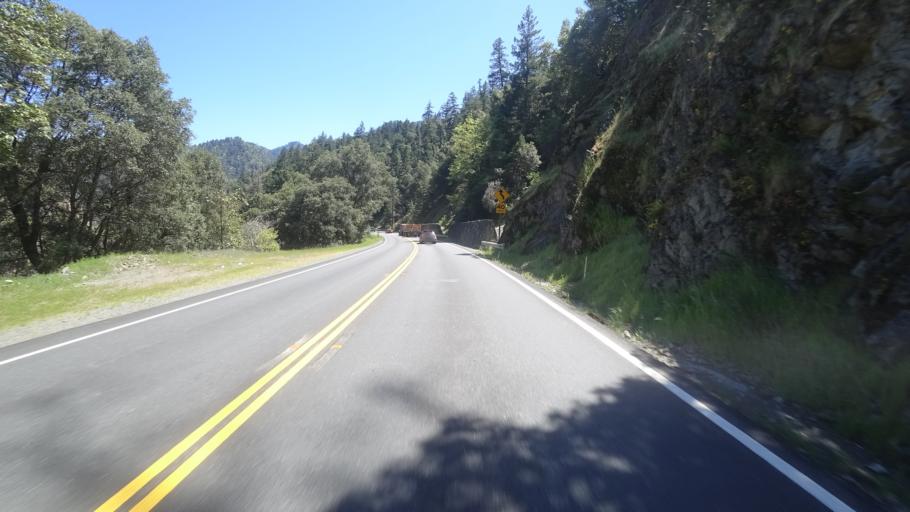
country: US
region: California
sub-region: Humboldt County
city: Willow Creek
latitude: 40.7915
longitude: -123.4556
